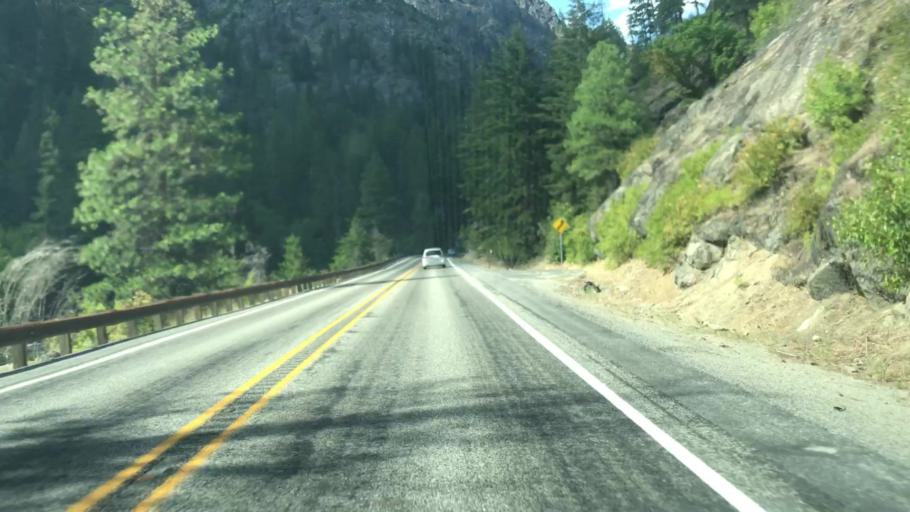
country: US
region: Washington
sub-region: Chelan County
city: Leavenworth
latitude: 47.6290
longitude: -120.7271
